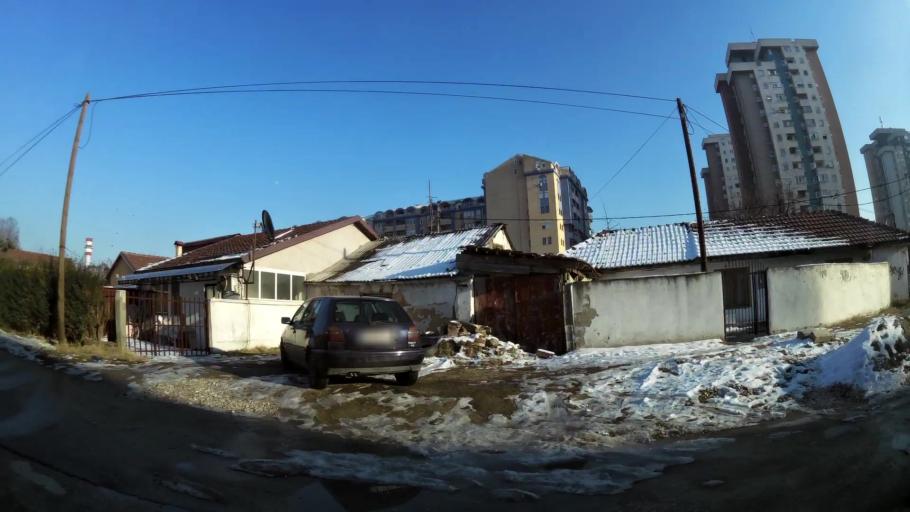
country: MK
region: Karpos
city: Skopje
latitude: 41.9925
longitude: 21.4484
